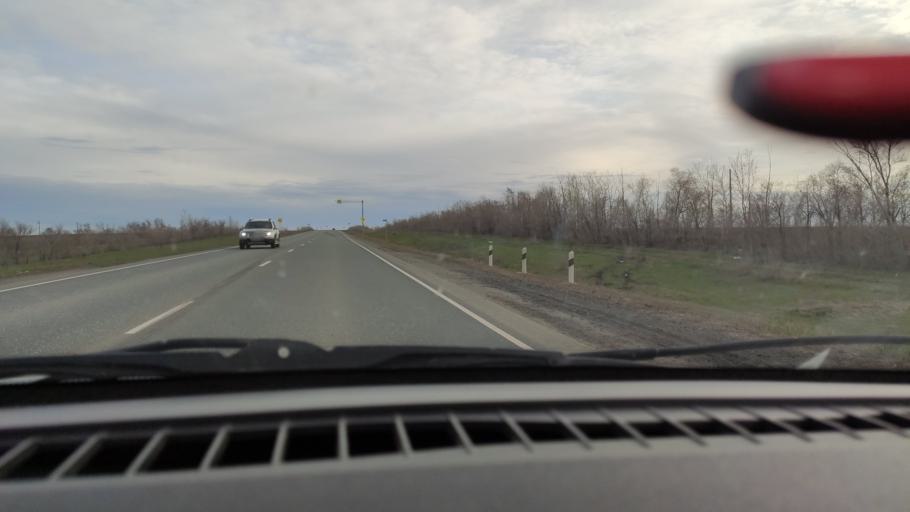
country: RU
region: Orenburg
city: Sakmara
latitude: 52.0826
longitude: 55.2670
